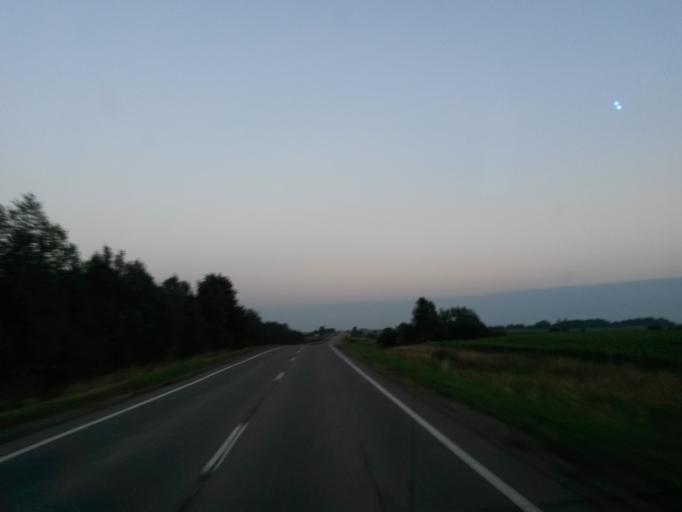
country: RU
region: Jaroslavl
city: Yaroslavl
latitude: 57.7816
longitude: 39.8437
